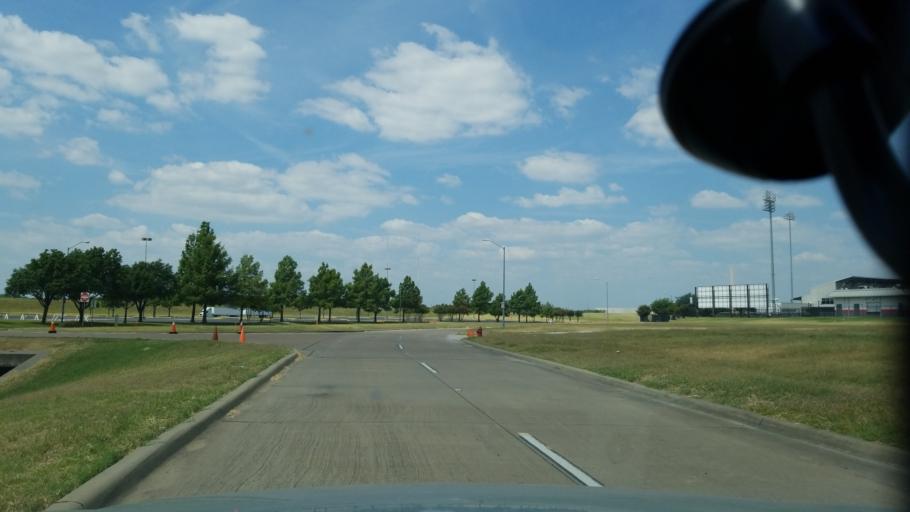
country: US
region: Texas
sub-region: Dallas County
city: Grand Prairie
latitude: 32.7679
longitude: -96.9838
